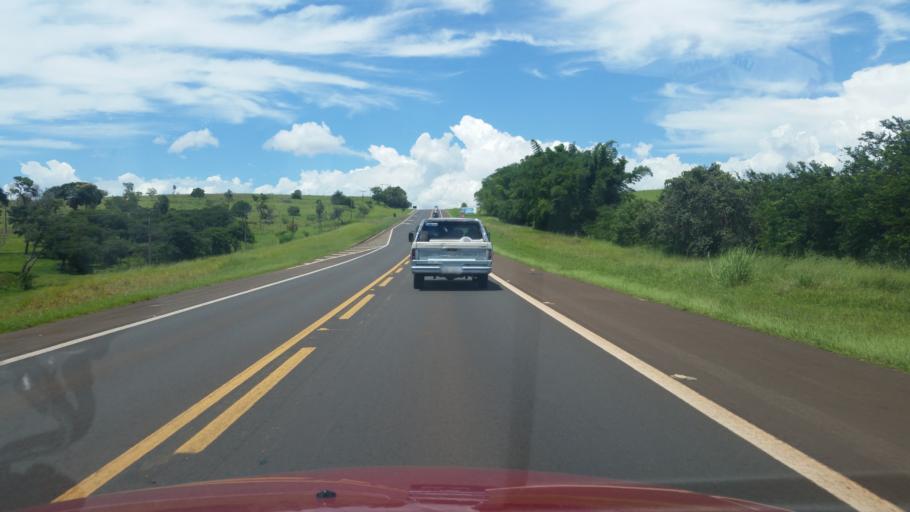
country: BR
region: Sao Paulo
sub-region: Itai
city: Itai
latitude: -23.2864
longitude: -49.0318
